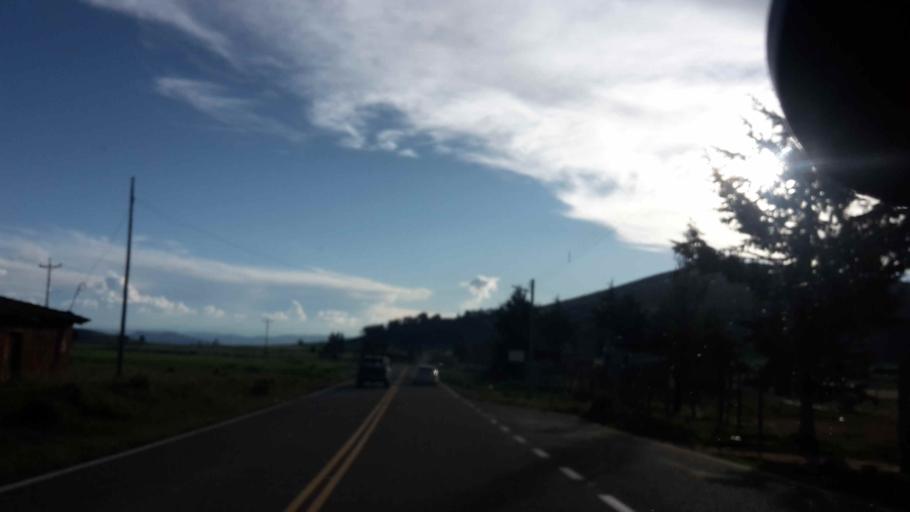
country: BO
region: Cochabamba
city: Arani
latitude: -17.5501
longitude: -65.6856
